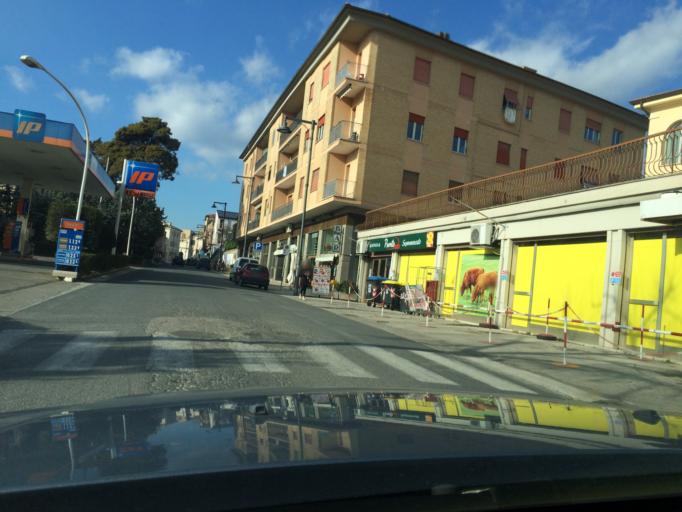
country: IT
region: Umbria
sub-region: Provincia di Terni
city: Amelia
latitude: 42.5522
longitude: 12.4194
